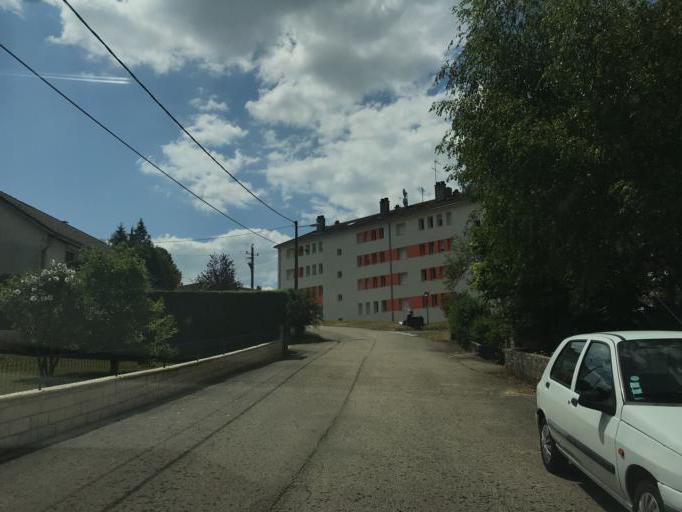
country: FR
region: Franche-Comte
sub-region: Departement du Jura
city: Clairvaux-les-Lacs
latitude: 46.5714
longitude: 5.7573
